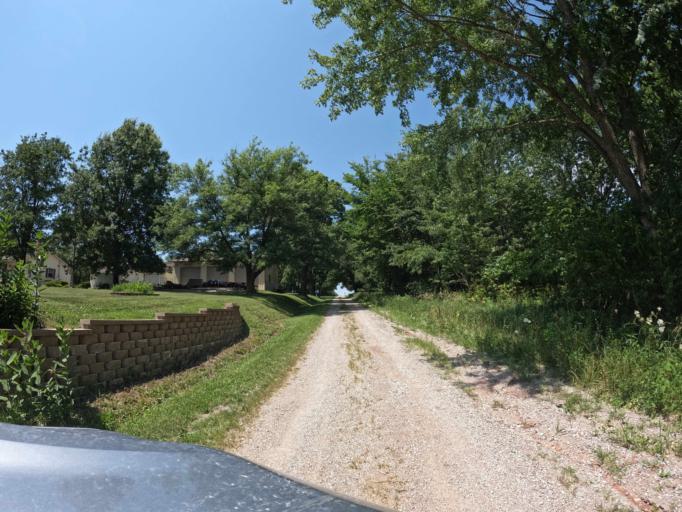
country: US
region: Iowa
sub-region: Appanoose County
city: Centerville
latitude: 40.7862
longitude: -92.9039
